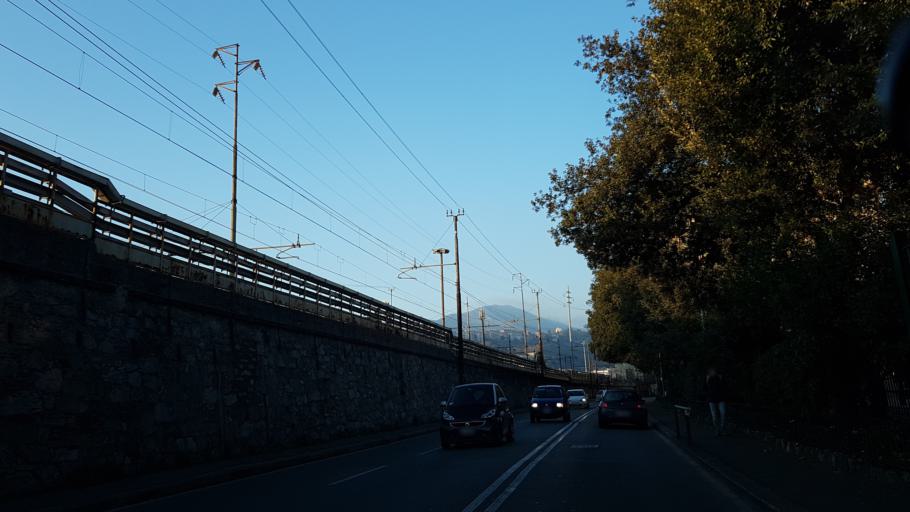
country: IT
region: Liguria
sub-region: Provincia di Genova
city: San Teodoro
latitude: 44.4158
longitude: 8.8854
